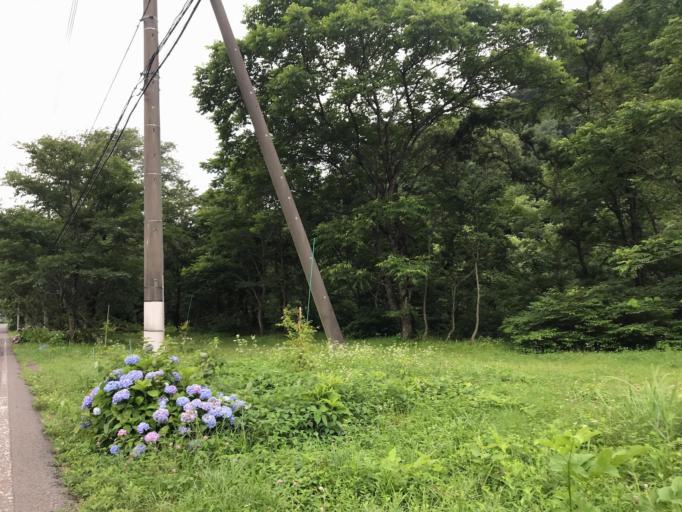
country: JP
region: Gunma
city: Numata
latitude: 36.8142
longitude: 138.9852
